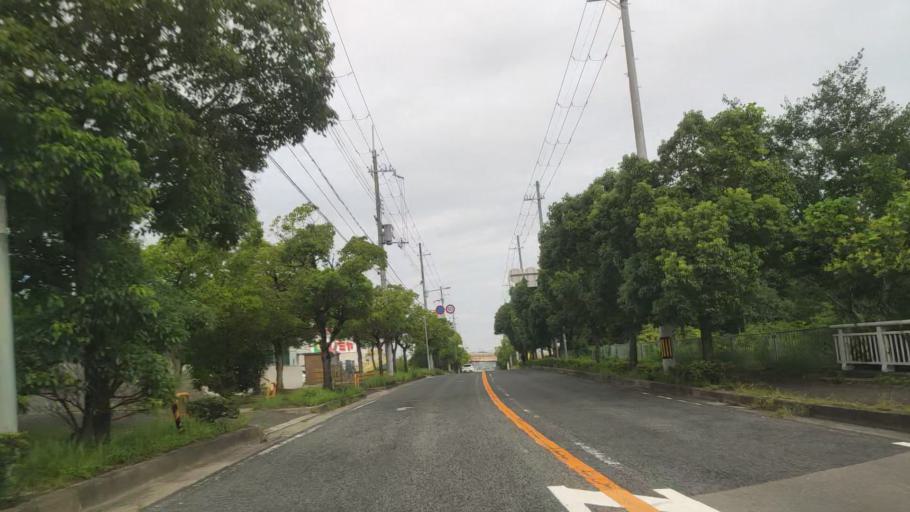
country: JP
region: Osaka
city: Tondabayashicho
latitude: 34.4259
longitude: 135.5717
